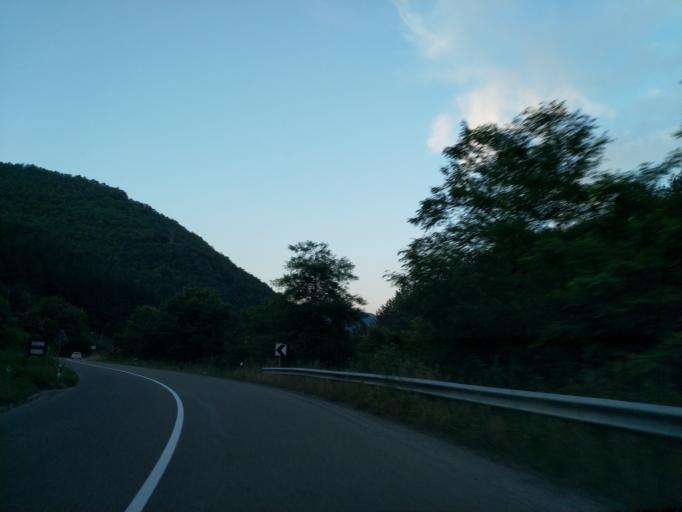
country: RS
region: Central Serbia
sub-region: Rasinski Okrug
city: Aleksandrovac
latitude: 43.3373
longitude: 20.9467
